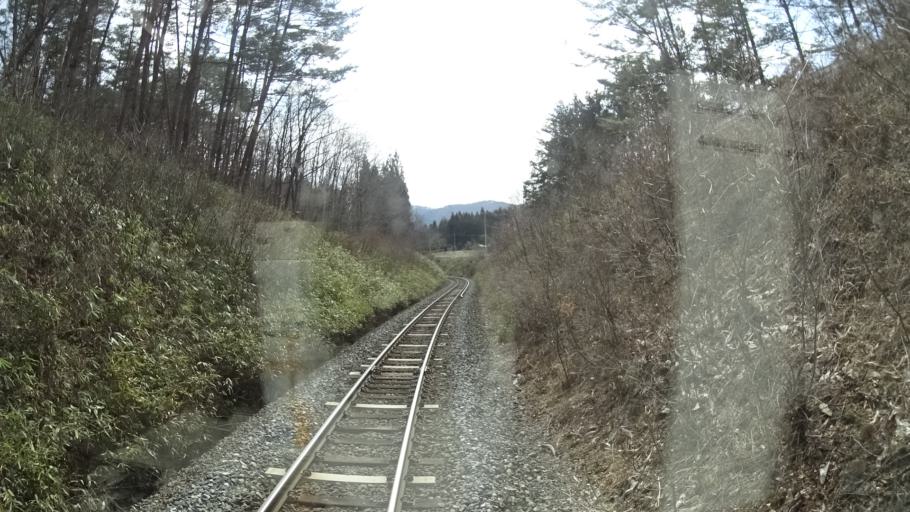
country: JP
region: Iwate
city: Tono
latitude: 39.3403
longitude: 141.3532
